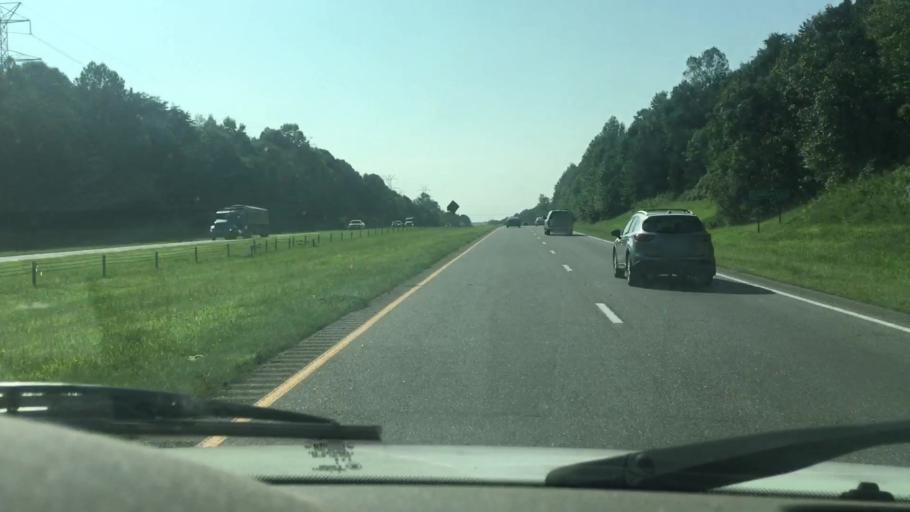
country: US
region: North Carolina
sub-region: Lincoln County
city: Lowesville
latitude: 35.3646
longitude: -80.9893
